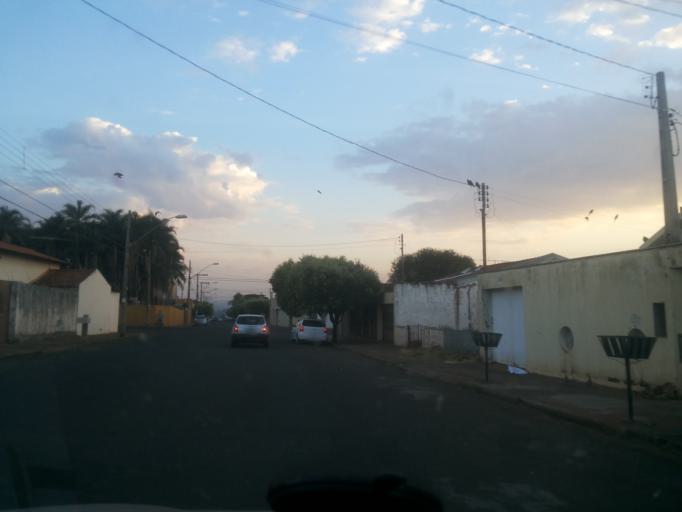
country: BR
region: Minas Gerais
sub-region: Ituiutaba
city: Ituiutaba
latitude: -18.9822
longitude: -49.4558
